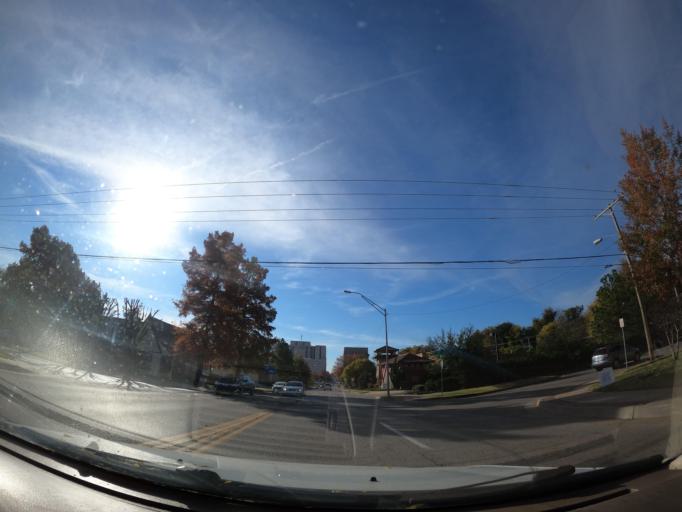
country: US
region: Oklahoma
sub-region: Tulsa County
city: Tulsa
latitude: 36.1395
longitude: -95.9671
